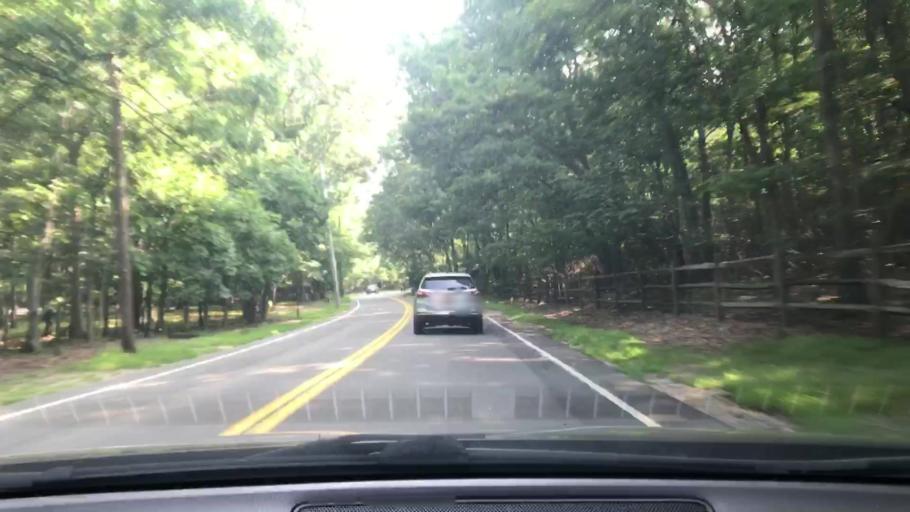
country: US
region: New York
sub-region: Suffolk County
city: Sag Harbor
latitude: 40.9842
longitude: -72.3121
